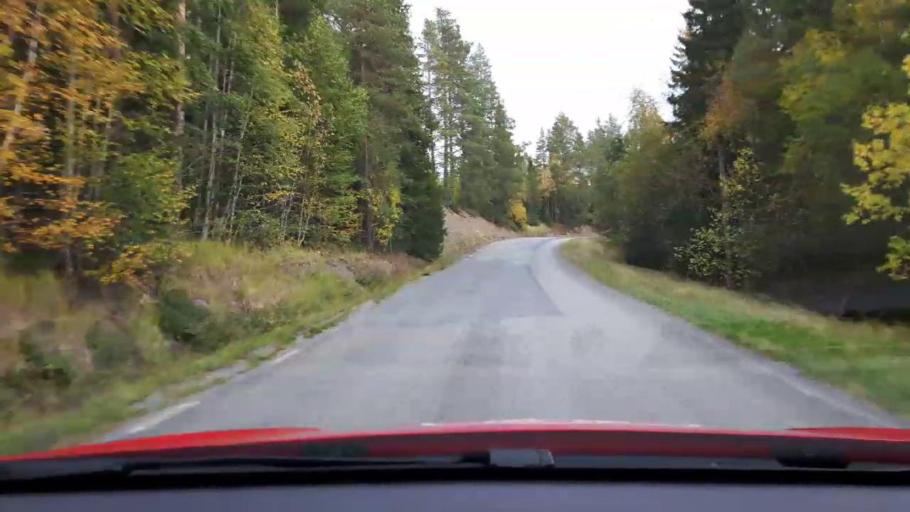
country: SE
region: Jaemtland
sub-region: Krokoms Kommun
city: Valla
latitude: 63.2617
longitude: 14.0010
